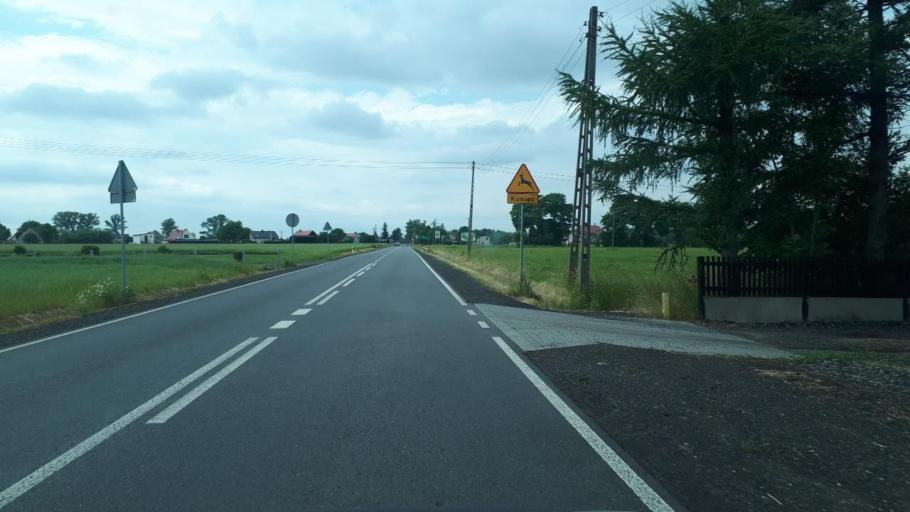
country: PL
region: Silesian Voivodeship
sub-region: Powiat tarnogorski
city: Krupski Mlyn
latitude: 50.5547
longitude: 18.5579
